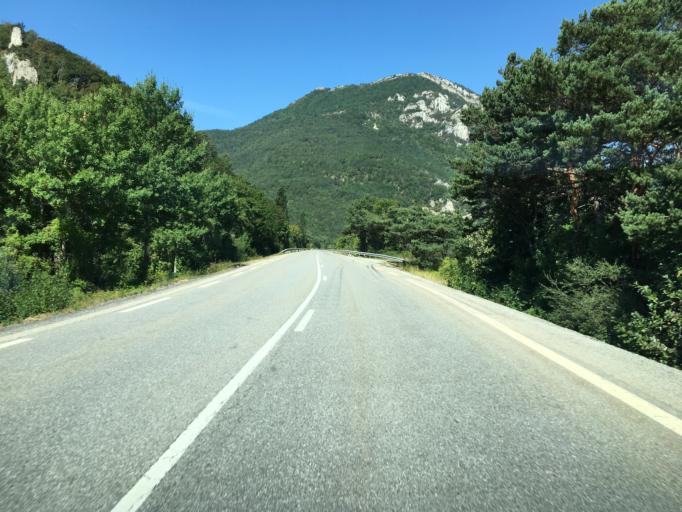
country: FR
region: Provence-Alpes-Cote d'Azur
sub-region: Departement des Hautes-Alpes
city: Veynes
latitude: 44.5937
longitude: 5.7156
